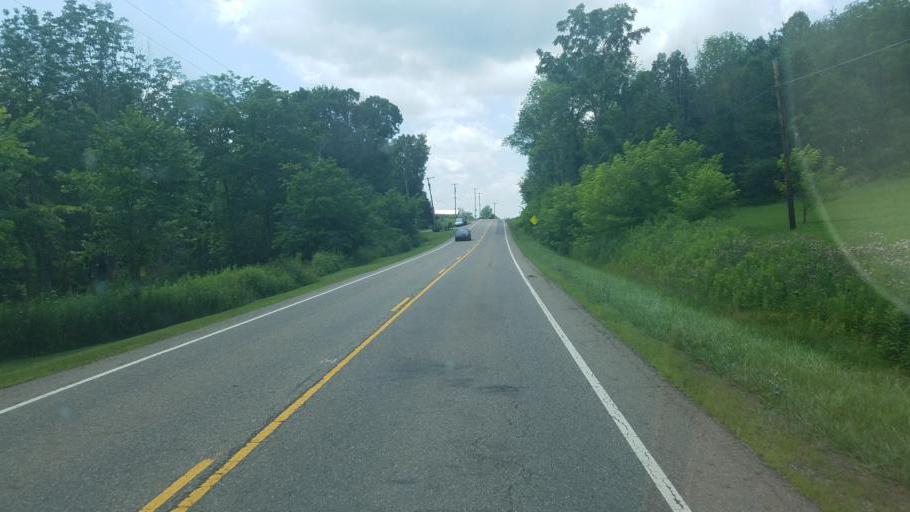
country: US
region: Ohio
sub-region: Stark County
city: Minerva
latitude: 40.7937
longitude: -81.1093
